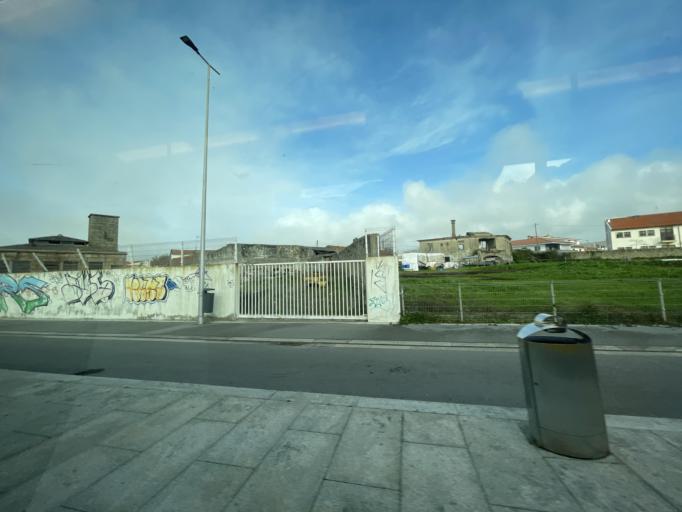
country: PT
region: Porto
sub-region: Povoa de Varzim
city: Povoa de Varzim
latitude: 41.3731
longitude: -8.7535
